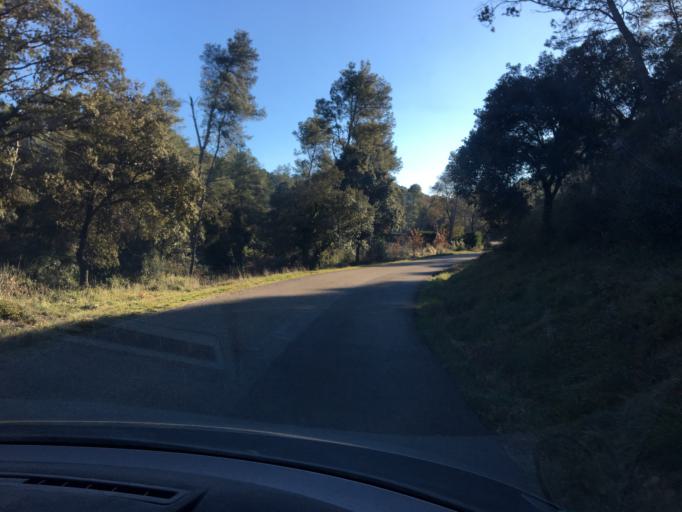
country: FR
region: Provence-Alpes-Cote d'Azur
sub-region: Departement des Bouches-du-Rhone
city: Saint-Remy-de-Provence
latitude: 43.7673
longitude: 4.7940
